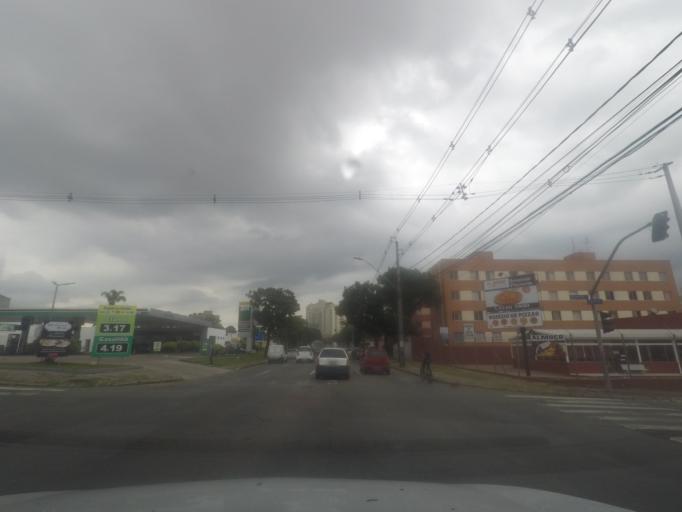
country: BR
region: Parana
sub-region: Curitiba
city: Curitiba
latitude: -25.4916
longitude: -49.2955
